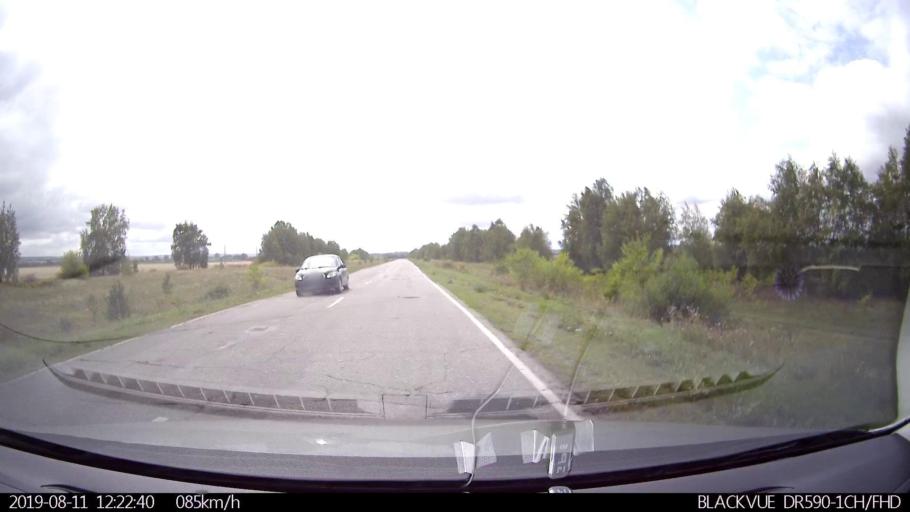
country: RU
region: Ulyanovsk
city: Ignatovka
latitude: 53.9047
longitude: 47.9512
